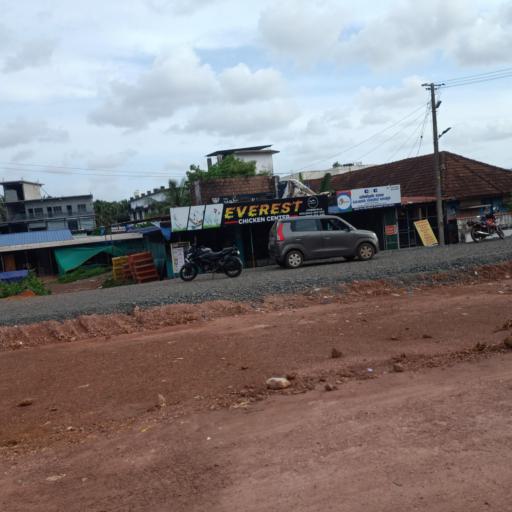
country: IN
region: Kerala
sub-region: Kasaragod District
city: Kasaragod
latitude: 12.5096
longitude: 75.0521
